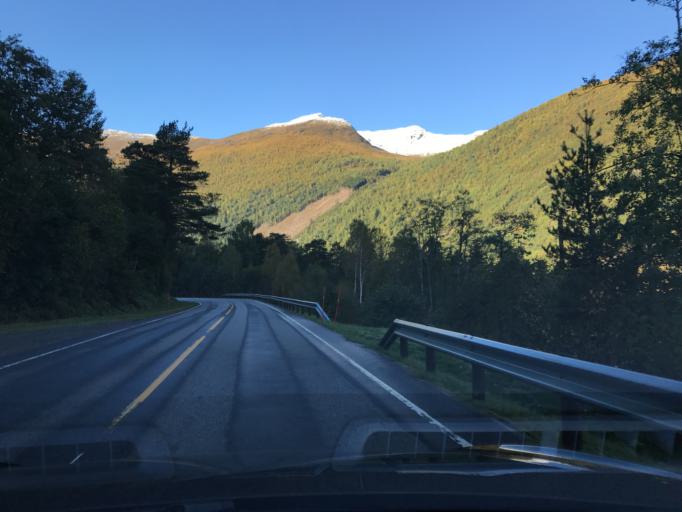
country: NO
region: More og Romsdal
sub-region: Norddal
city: Valldal
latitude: 62.3138
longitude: 7.2798
